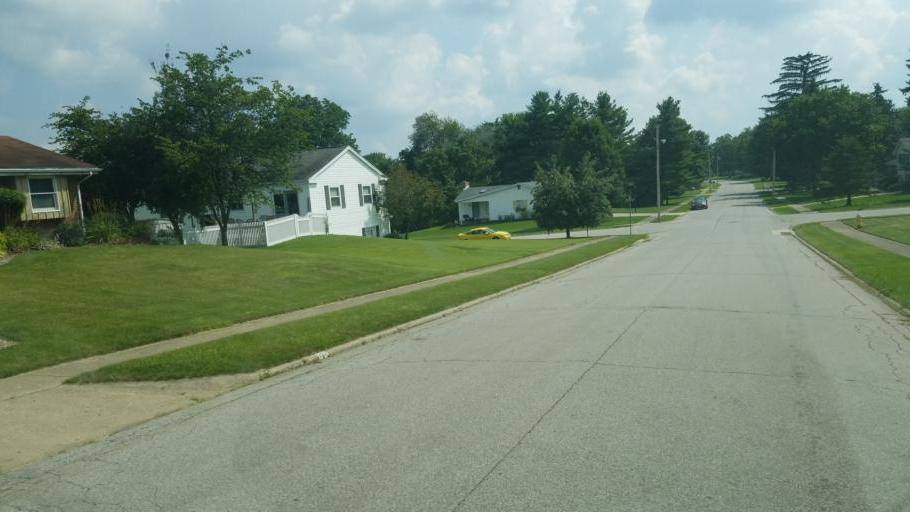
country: US
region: Ohio
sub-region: Richland County
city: Lexington
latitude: 40.6872
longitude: -82.5978
